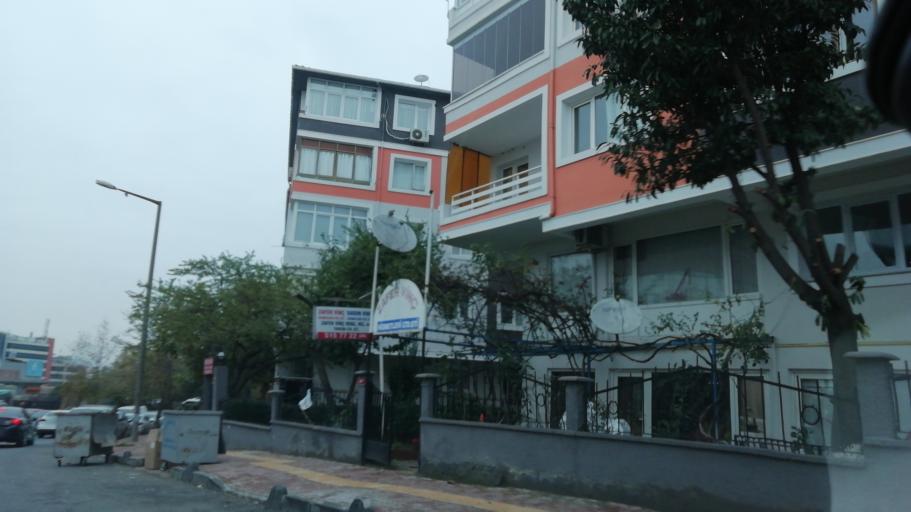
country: TR
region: Istanbul
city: Mahmutbey
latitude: 41.0179
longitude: 28.8224
